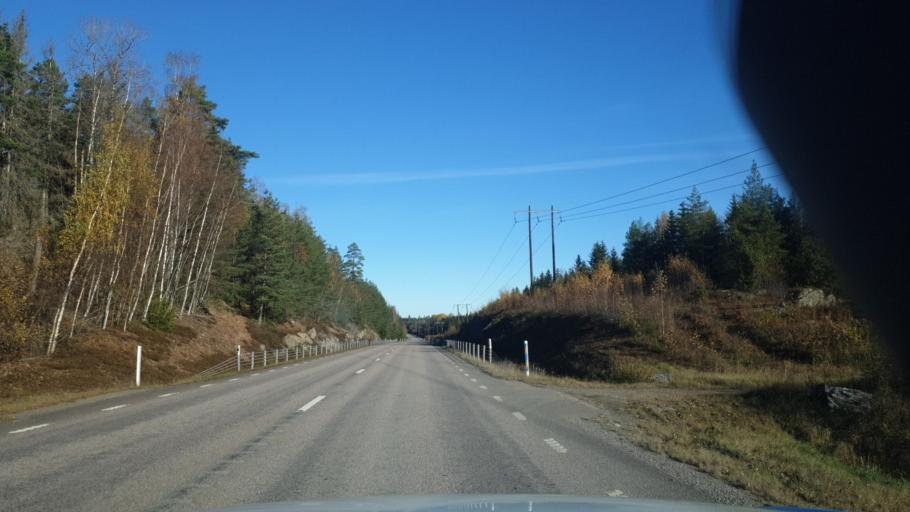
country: SE
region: Vaermland
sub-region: Karlstads Kommun
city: Edsvalla
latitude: 59.4198
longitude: 13.1893
